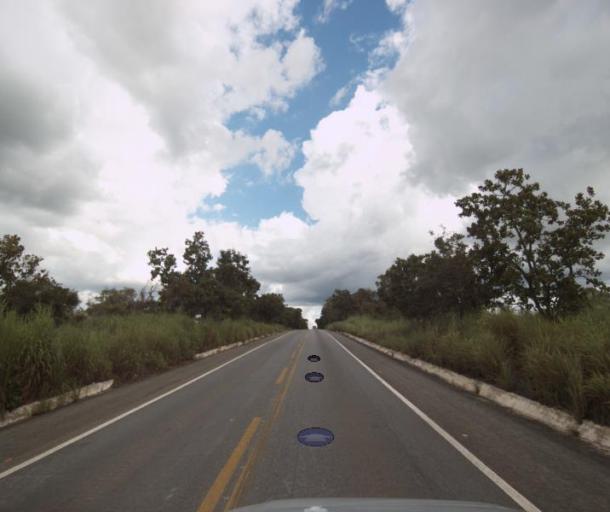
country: BR
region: Goias
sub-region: Porangatu
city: Porangatu
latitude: -13.2493
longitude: -49.1390
